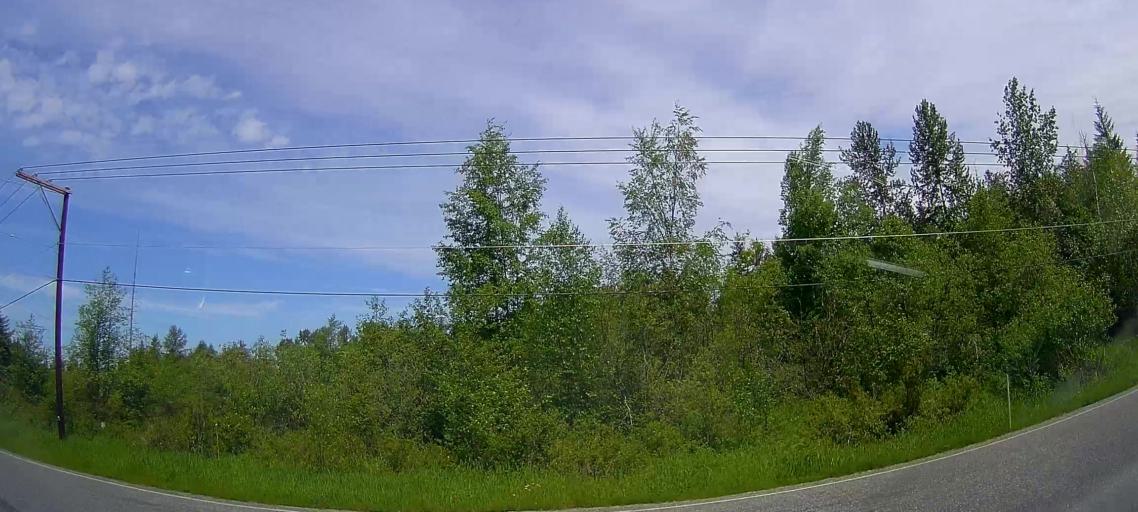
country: US
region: Washington
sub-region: Snohomish County
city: Bryant
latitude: 48.3278
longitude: -122.1599
